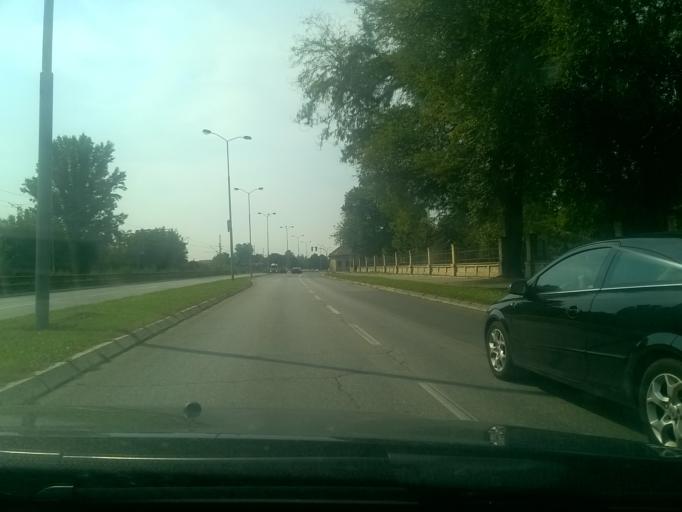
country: RS
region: Autonomna Pokrajina Vojvodina
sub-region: Juznobanatski Okrug
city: Pancevo
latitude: 44.8629
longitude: 20.6578
